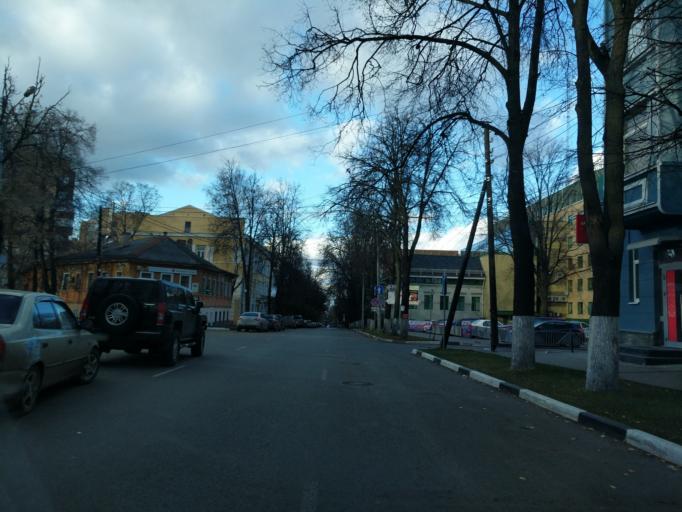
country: RU
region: Nizjnij Novgorod
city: Nizhniy Novgorod
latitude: 56.3103
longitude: 43.9913
